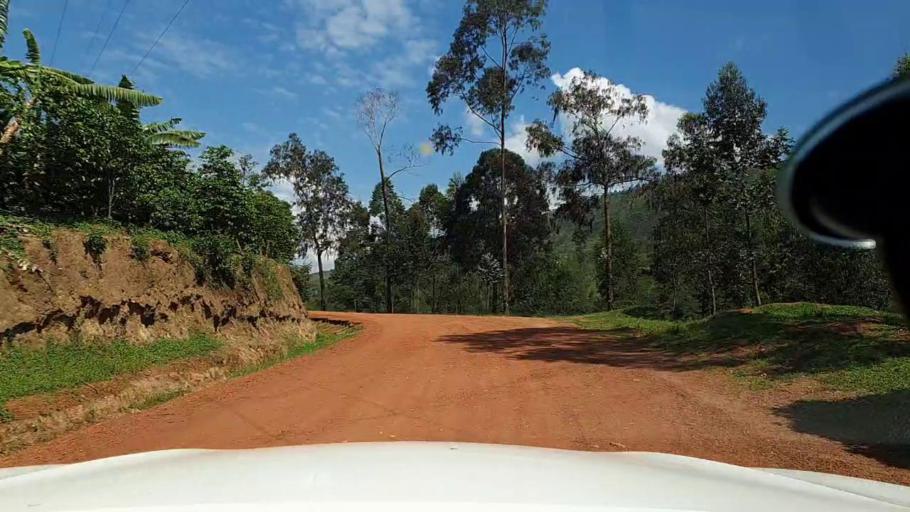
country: RW
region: Kigali
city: Kigali
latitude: -1.7853
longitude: 29.8815
